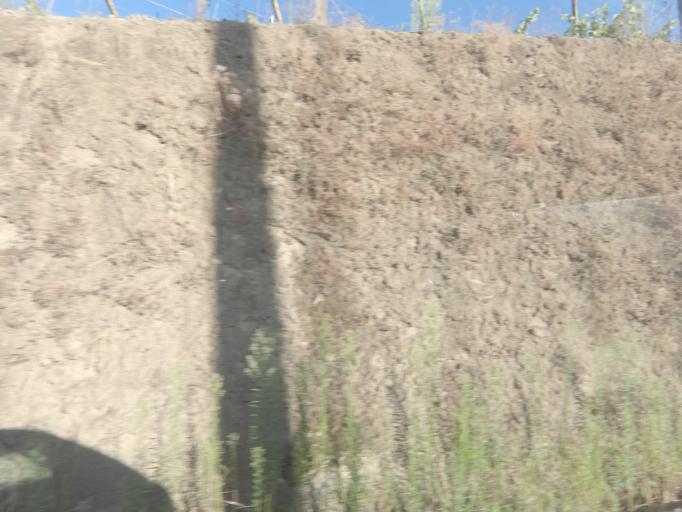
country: PT
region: Vila Real
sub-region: Santa Marta de Penaguiao
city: Santa Marta de Penaguiao
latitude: 41.1983
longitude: -7.7711
